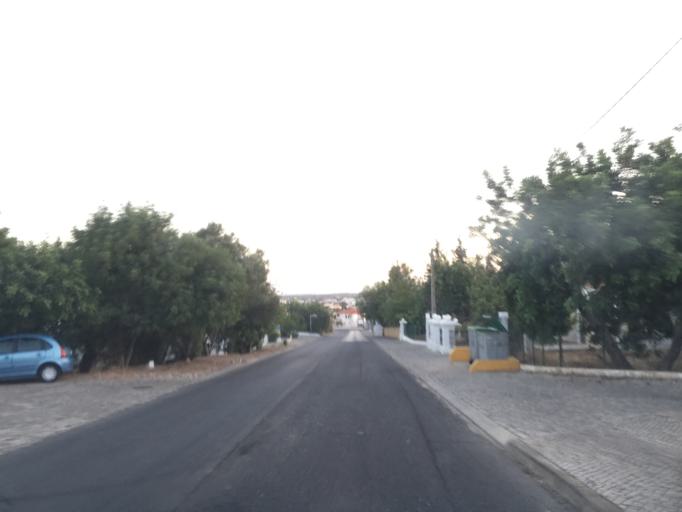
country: PT
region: Faro
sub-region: Loule
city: Almancil
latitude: 37.0990
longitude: -8.0235
